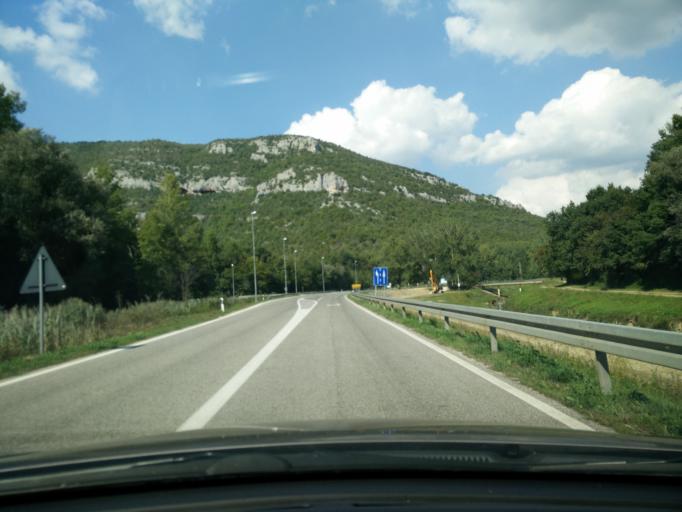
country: HR
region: Istarska
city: Buzet
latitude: 45.3754
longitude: 13.8891
